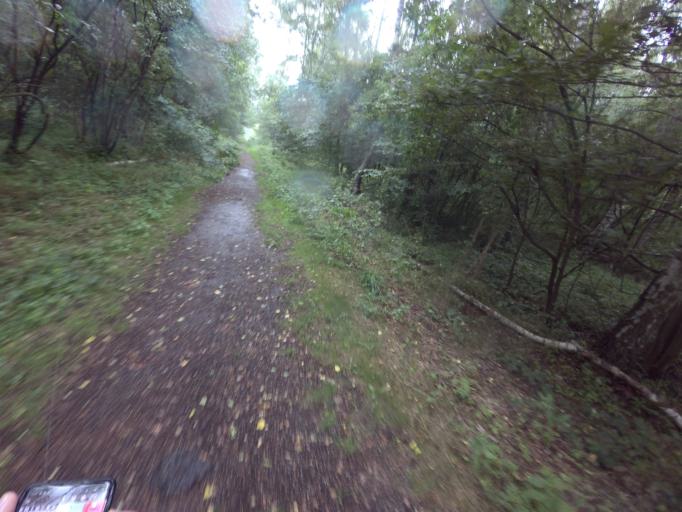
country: BE
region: Wallonia
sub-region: Province de Liege
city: Plombieres
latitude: 50.7339
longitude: 5.9664
